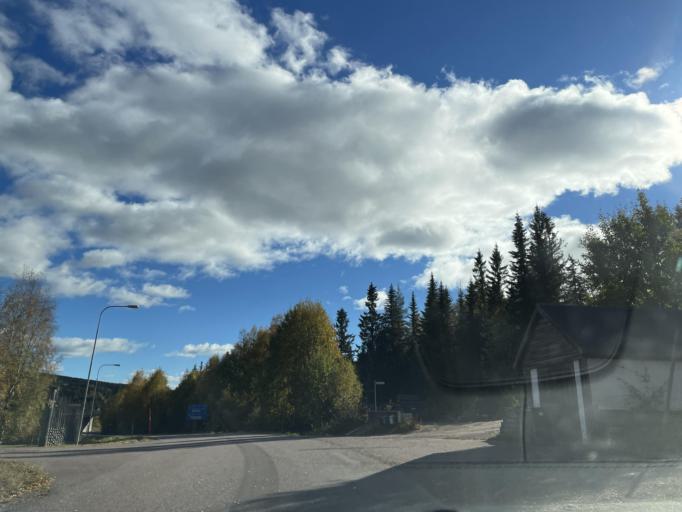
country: SE
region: Dalarna
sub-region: Malung-Saelens kommun
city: Malung
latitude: 61.1499
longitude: 13.2641
